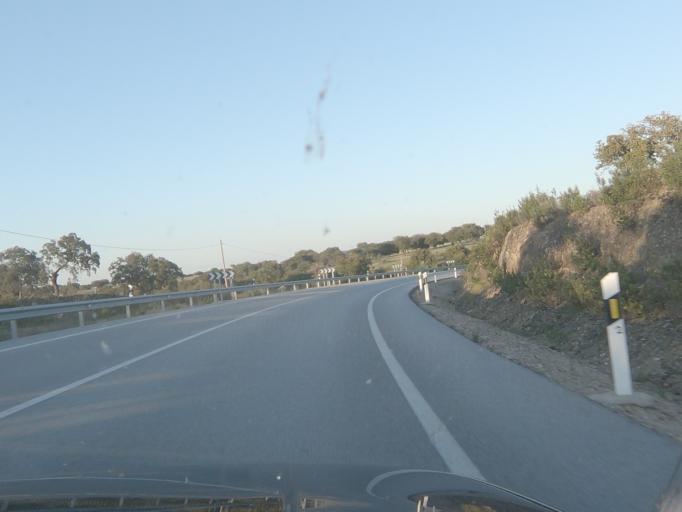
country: ES
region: Extremadura
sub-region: Provincia de Caceres
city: Carbajo
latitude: 39.4982
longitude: -7.1831
